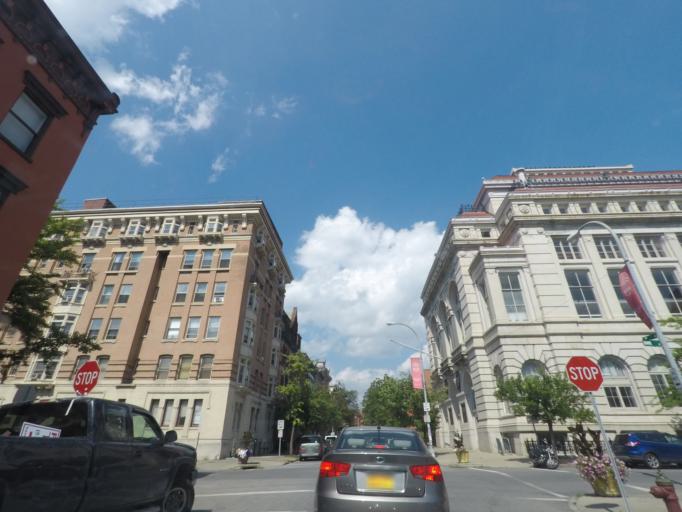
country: US
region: New York
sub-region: Rensselaer County
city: Troy
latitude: 42.7297
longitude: -73.6917
